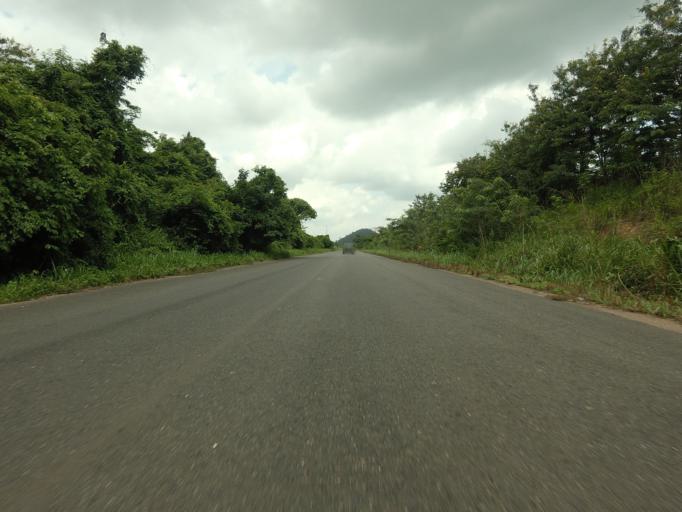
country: GH
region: Volta
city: Ho
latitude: 6.4389
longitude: 0.1721
